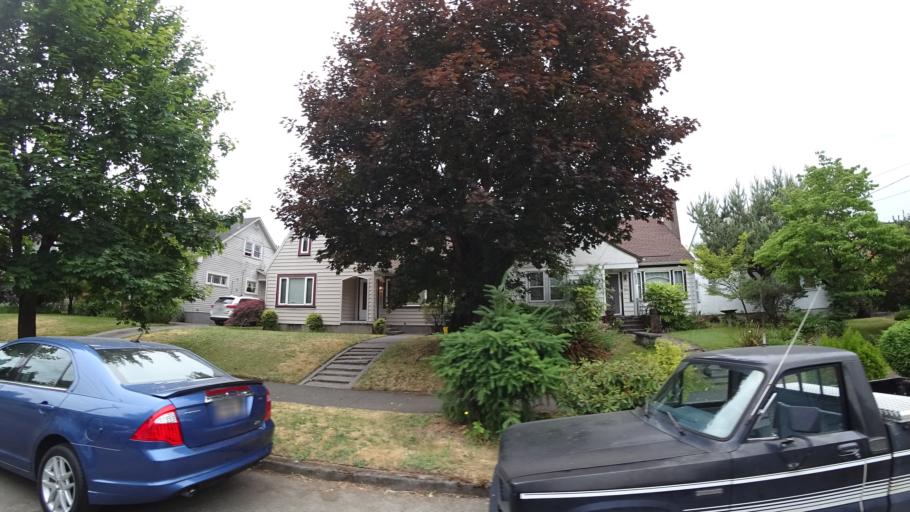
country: US
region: Oregon
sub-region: Multnomah County
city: Portland
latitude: 45.5727
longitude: -122.6993
